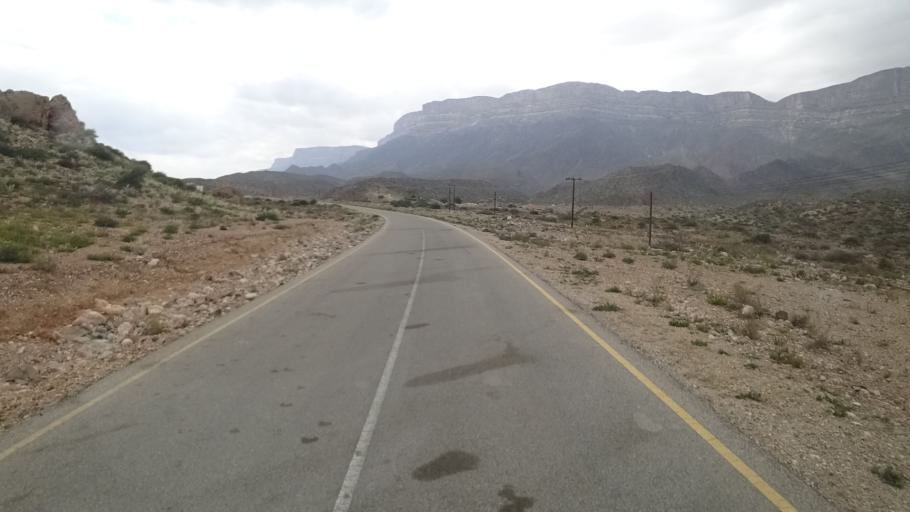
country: OM
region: Zufar
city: Salalah
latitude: 17.1740
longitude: 54.9666
